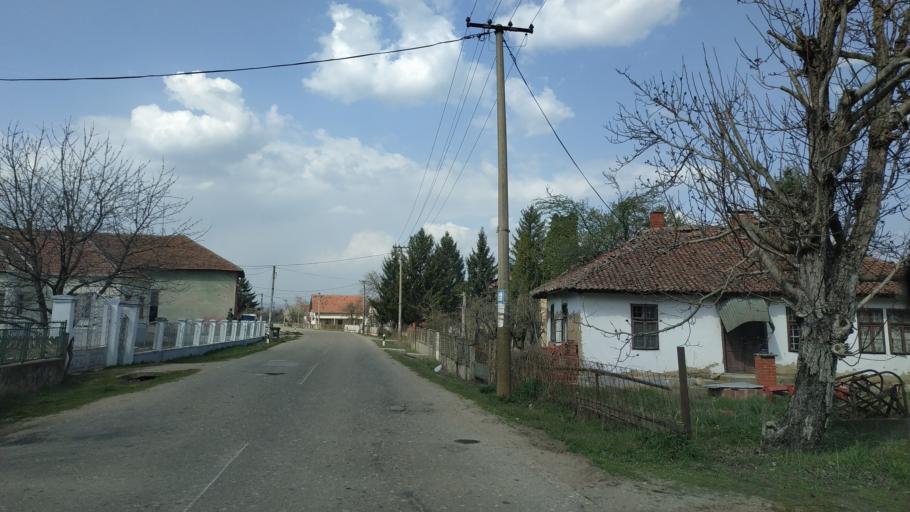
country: RS
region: Central Serbia
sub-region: Nisavski Okrug
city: Razanj
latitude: 43.5790
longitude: 21.5744
